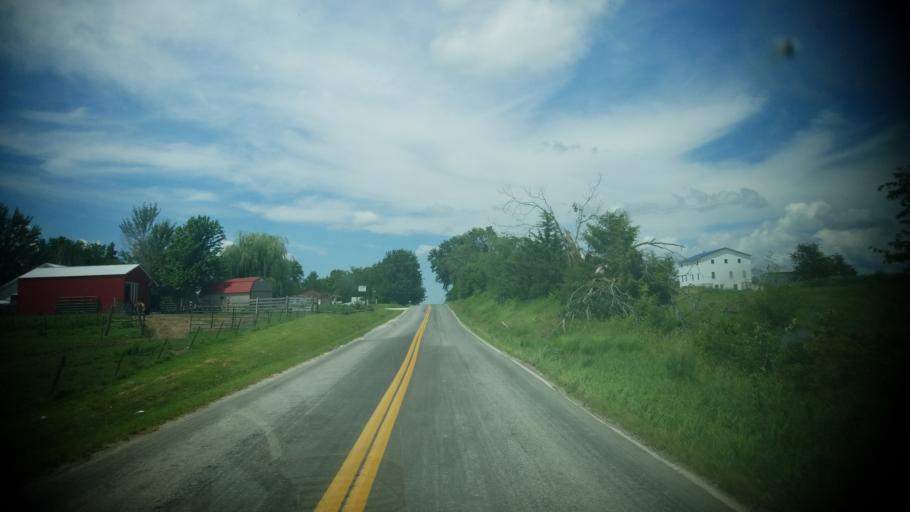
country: US
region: Missouri
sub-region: Audrain County
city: Vandalia
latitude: 39.3190
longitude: -91.3452
